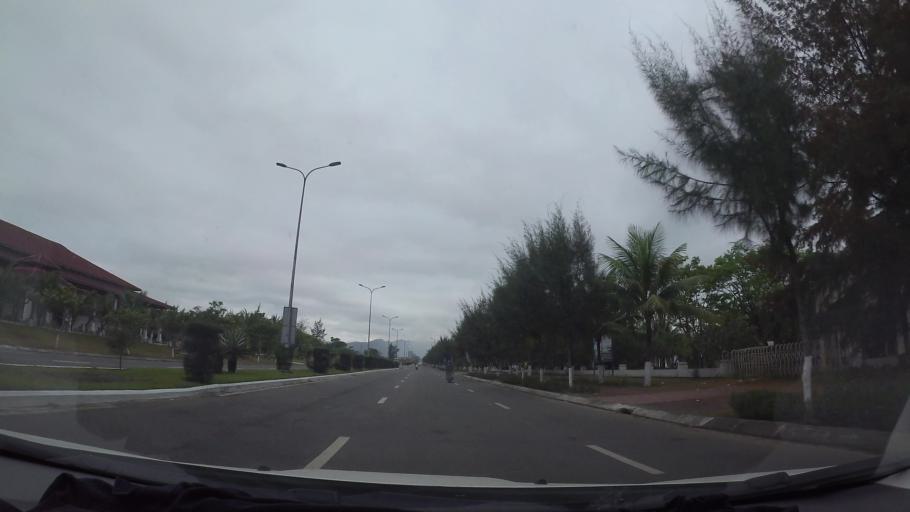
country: VN
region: Da Nang
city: Lien Chieu
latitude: 16.0945
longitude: 108.1468
